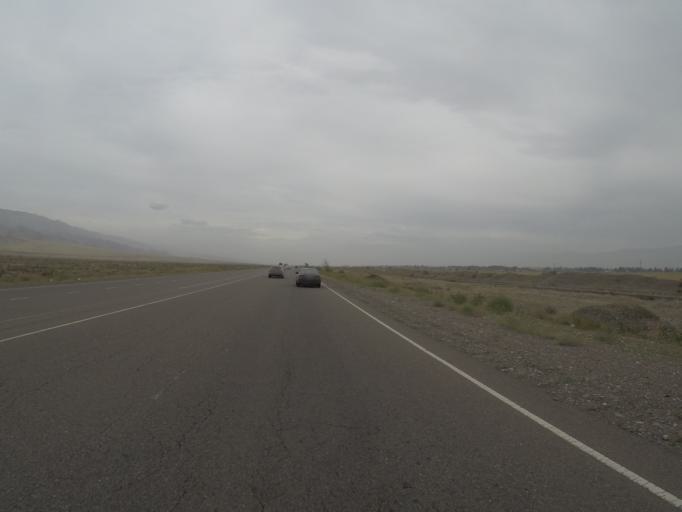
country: KG
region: Chuy
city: Tokmok
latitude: 42.8299
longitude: 75.4970
